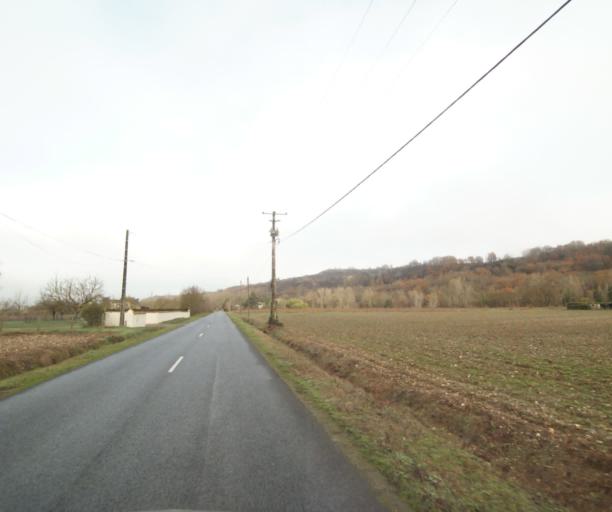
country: FR
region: Midi-Pyrenees
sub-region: Departement du Tarn-et-Garonne
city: Nohic
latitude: 43.8921
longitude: 1.4731
